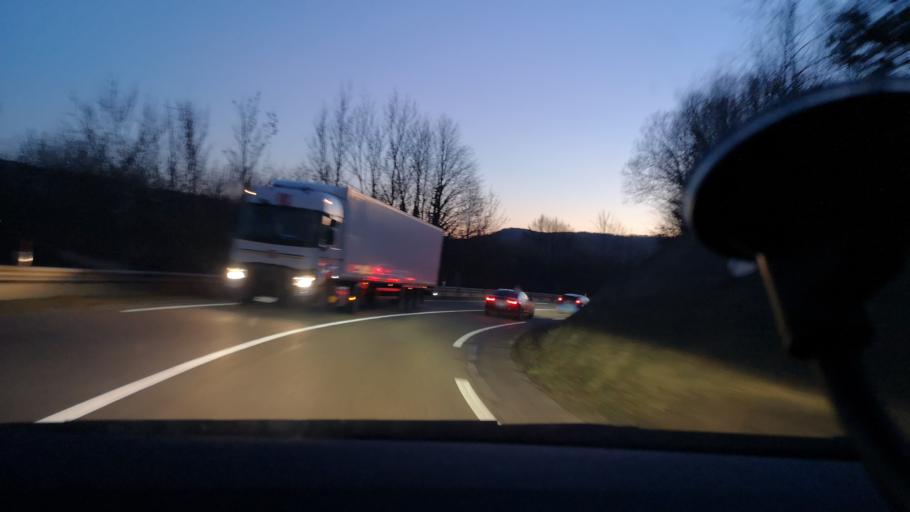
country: FR
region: Franche-Comte
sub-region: Departement du Jura
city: Champagnole
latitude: 46.7533
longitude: 5.9337
